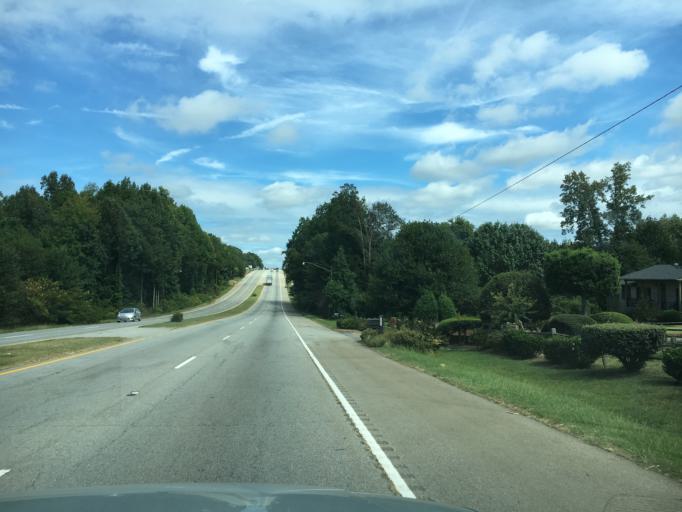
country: US
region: South Carolina
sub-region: Spartanburg County
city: Lyman
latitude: 34.9556
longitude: -82.1401
